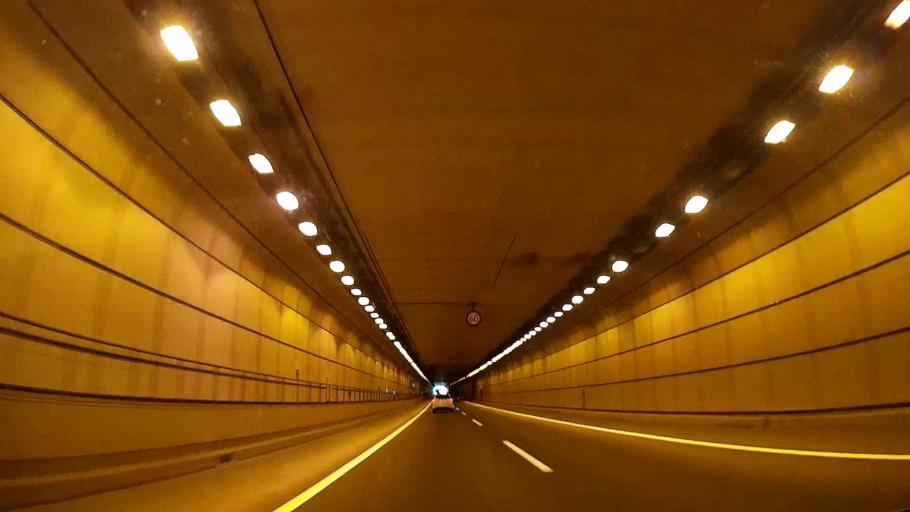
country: JP
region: Kanagawa
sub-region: Kawasaki-shi
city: Kawasaki
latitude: 35.5606
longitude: 139.7760
